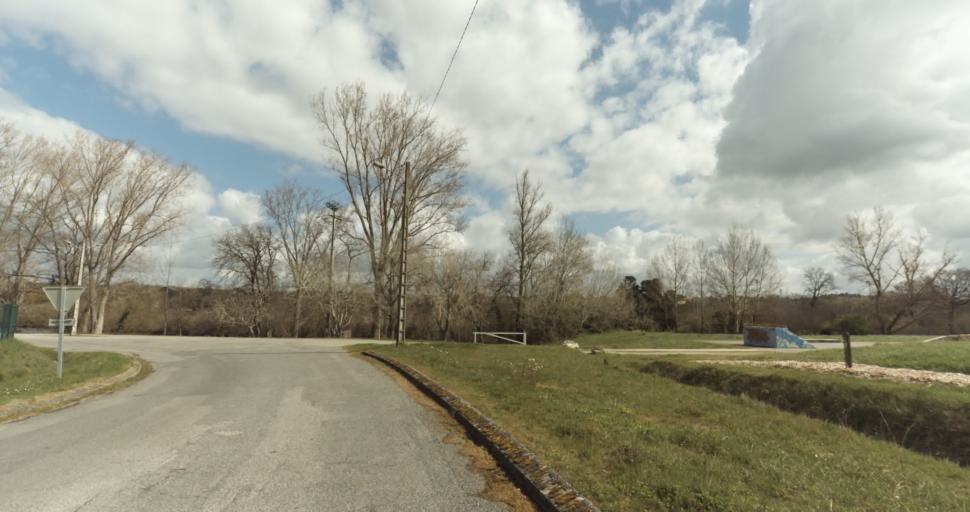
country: FR
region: Midi-Pyrenees
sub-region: Departement de la Haute-Garonne
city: Auterive
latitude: 43.3457
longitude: 1.4747
